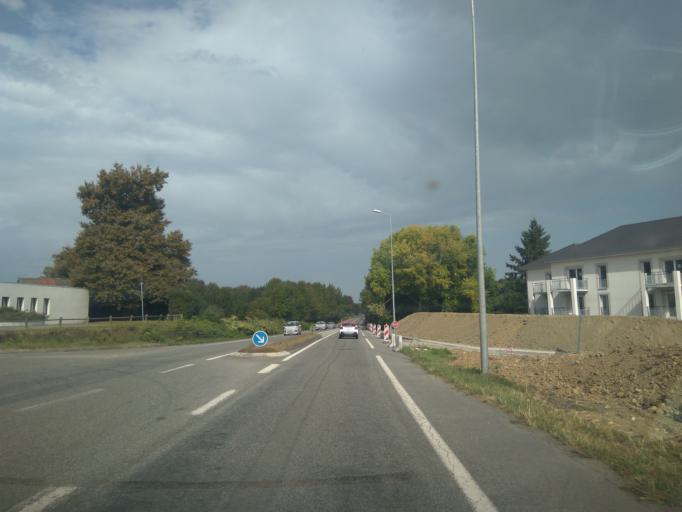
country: FR
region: Aquitaine
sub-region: Departement des Pyrenees-Atlantiques
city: Artiguelouve
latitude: 43.3180
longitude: -0.4628
